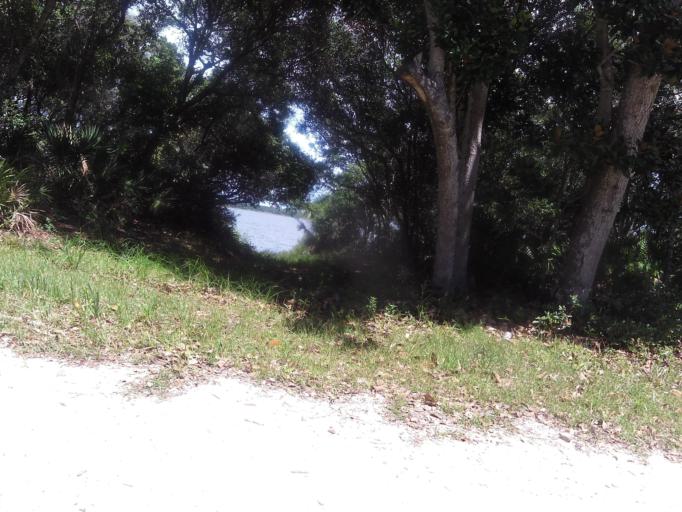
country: US
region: Florida
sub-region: Saint Johns County
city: Villano Beach
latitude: 30.0399
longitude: -81.3372
